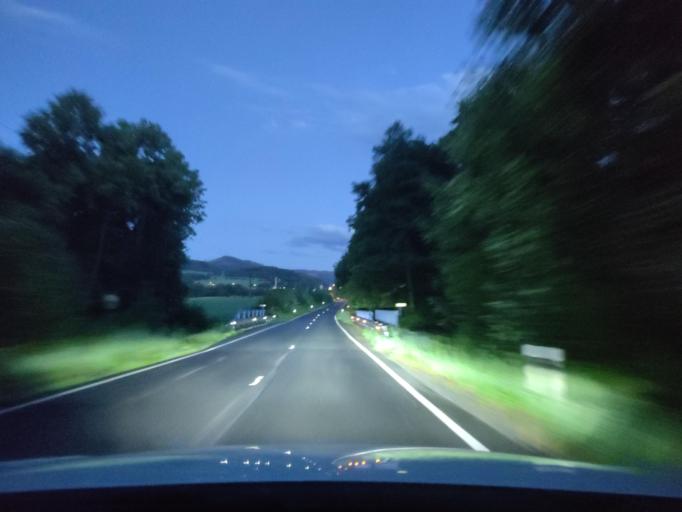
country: CZ
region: Olomoucky
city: Zlate Hory
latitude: 50.2806
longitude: 17.3899
